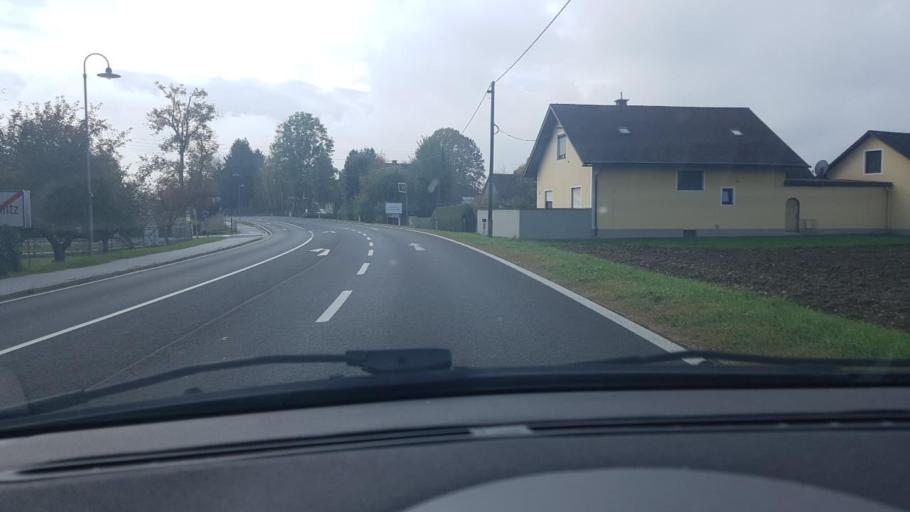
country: AT
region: Styria
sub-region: Politischer Bezirk Leibnitz
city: Kaindorf an der Sulm
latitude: 46.7892
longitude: 15.5617
